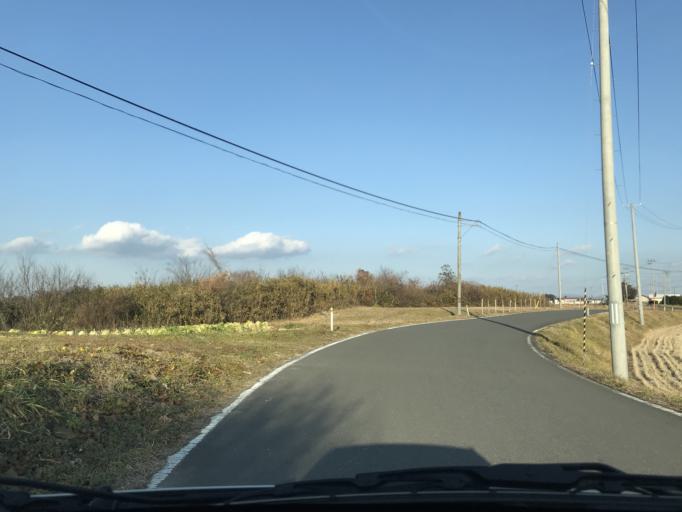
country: JP
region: Miyagi
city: Wakuya
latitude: 38.6952
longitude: 141.1195
